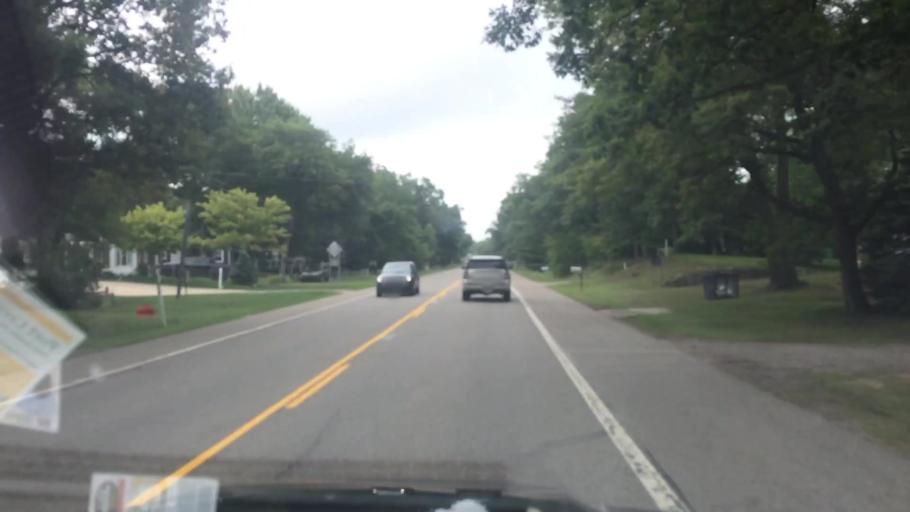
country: US
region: Michigan
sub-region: Huron County
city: Pigeon
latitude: 43.9673
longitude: -83.2608
